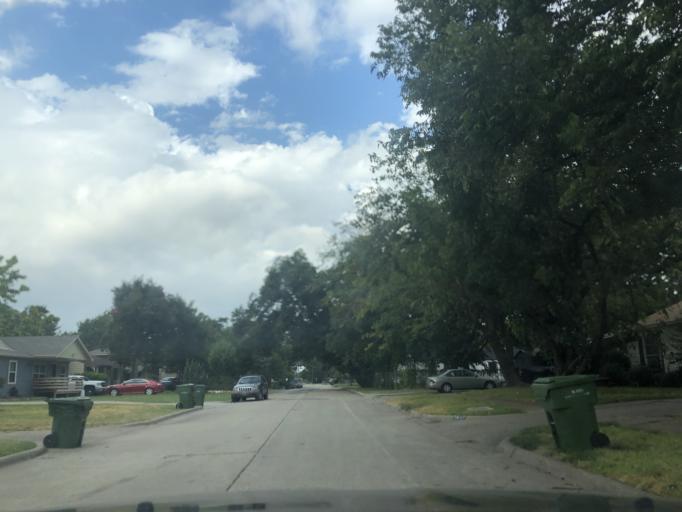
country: US
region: Texas
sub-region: Dallas County
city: Garland
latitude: 32.8829
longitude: -96.6527
